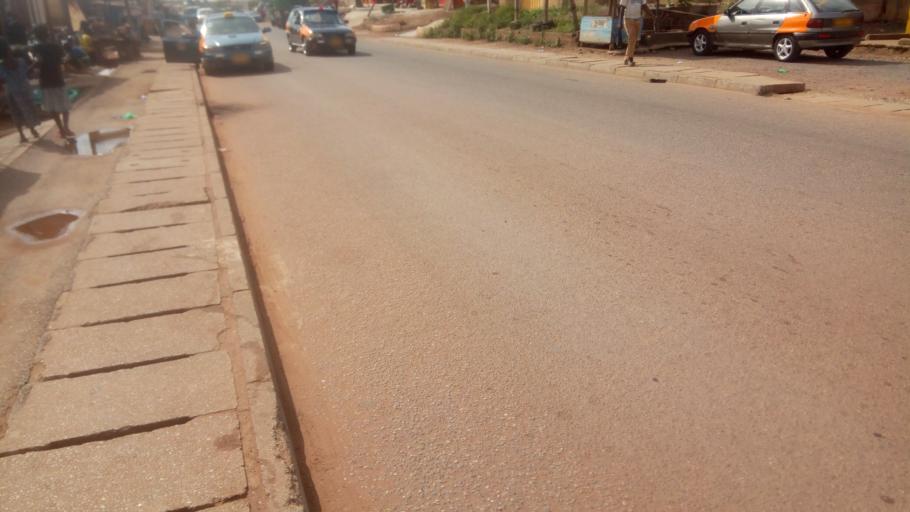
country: GH
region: Ashanti
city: Obuasi
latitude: 6.2084
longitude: -1.6841
